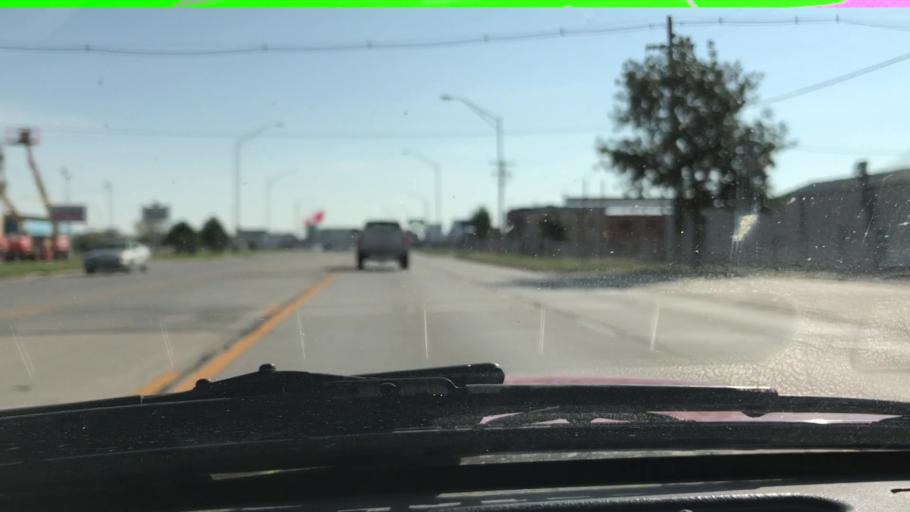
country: US
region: Nebraska
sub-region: Lancaster County
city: Lincoln
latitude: 40.8137
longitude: -96.7282
